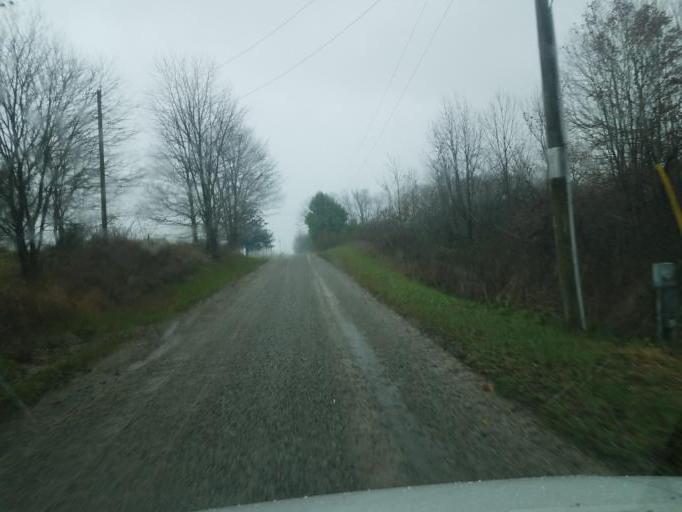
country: US
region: Ohio
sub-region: Morrow County
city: Mount Gilead
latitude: 40.5360
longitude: -82.7035
